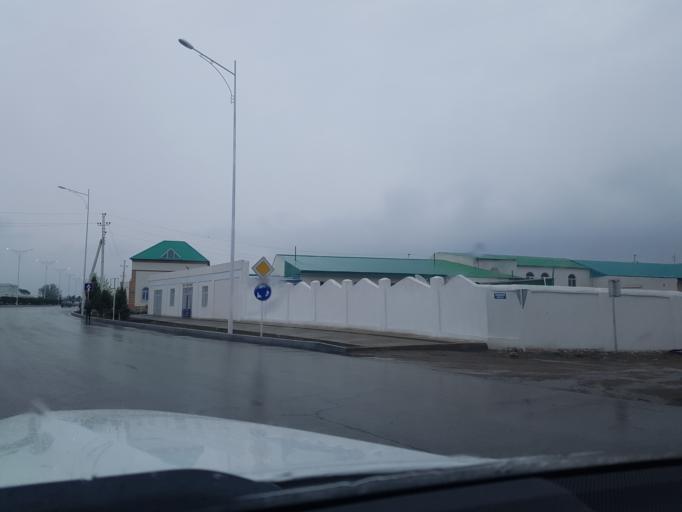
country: TM
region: Lebap
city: Turkmenabat
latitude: 39.0204
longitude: 63.5977
